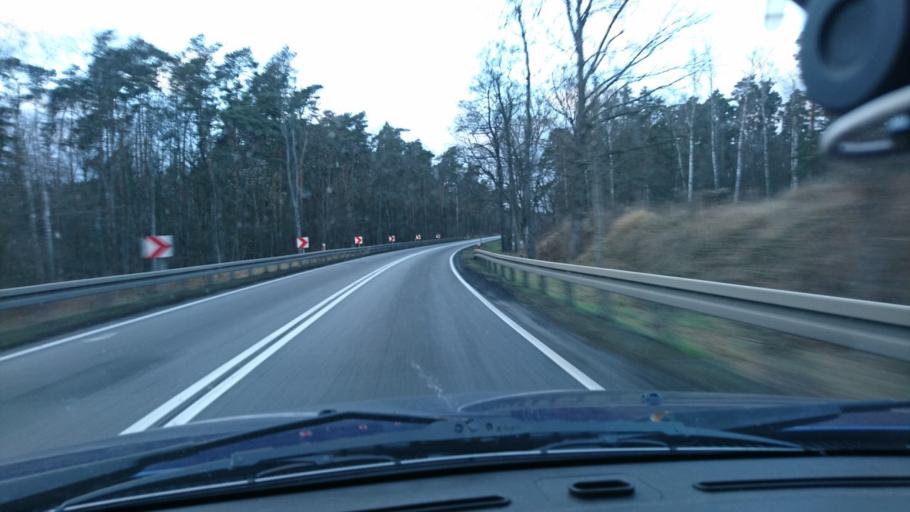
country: PL
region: Greater Poland Voivodeship
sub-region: Powiat kepinski
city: Kepno
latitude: 51.3277
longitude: 17.9619
